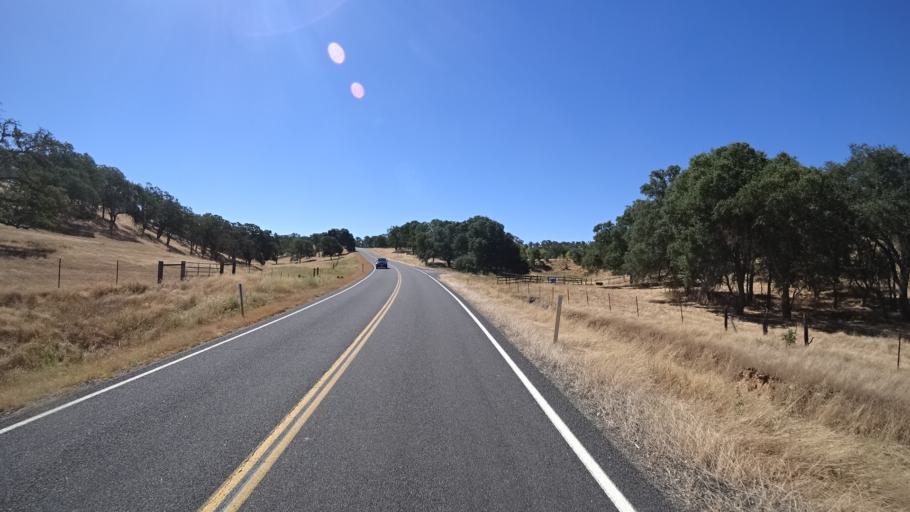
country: US
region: California
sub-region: Calaveras County
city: Rancho Calaveras
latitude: 38.0729
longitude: -120.8691
